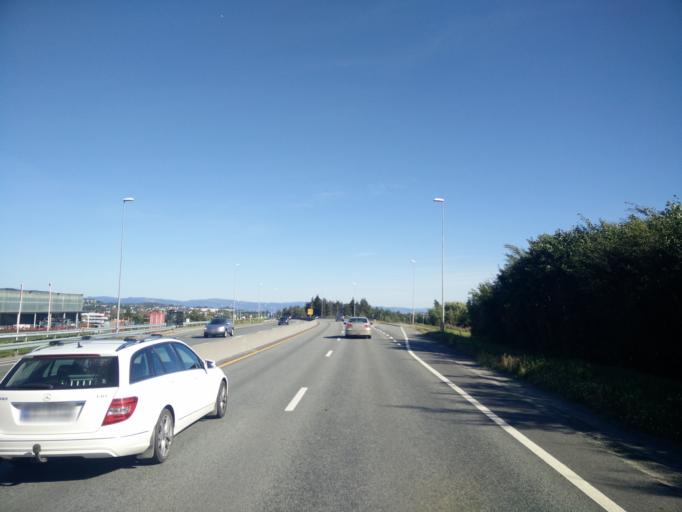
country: NO
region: Sor-Trondelag
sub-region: Trondheim
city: Trondheim
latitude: 63.3681
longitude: 10.3792
